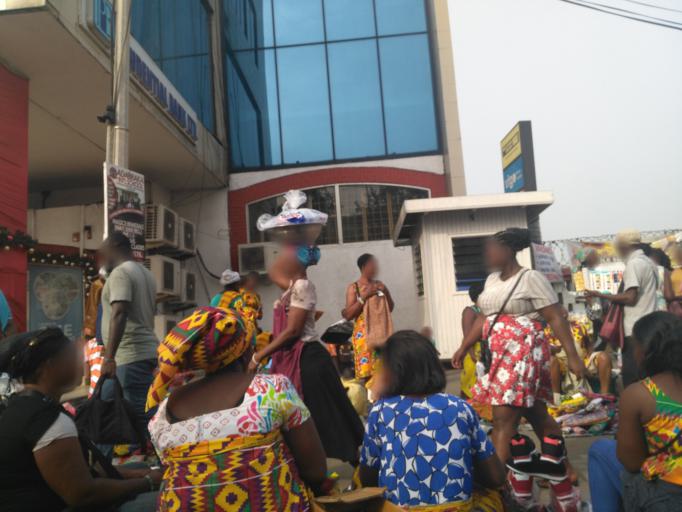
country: GH
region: Greater Accra
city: Accra
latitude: 5.5534
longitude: -0.2111
